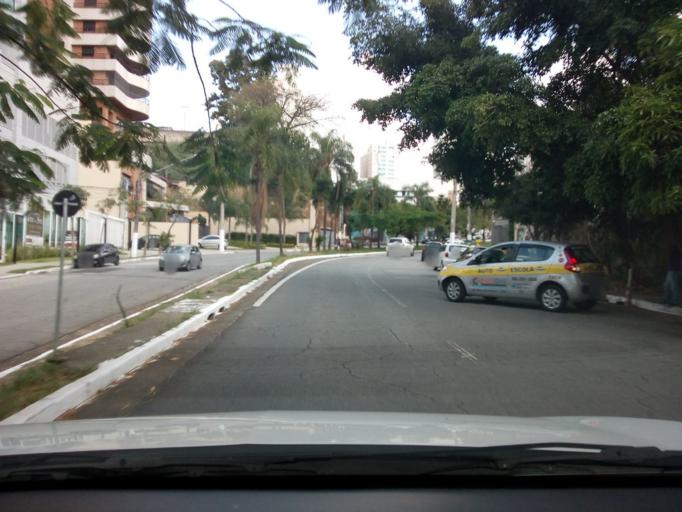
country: BR
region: Sao Paulo
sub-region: Sao Paulo
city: Sao Paulo
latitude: -23.5845
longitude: -46.6292
